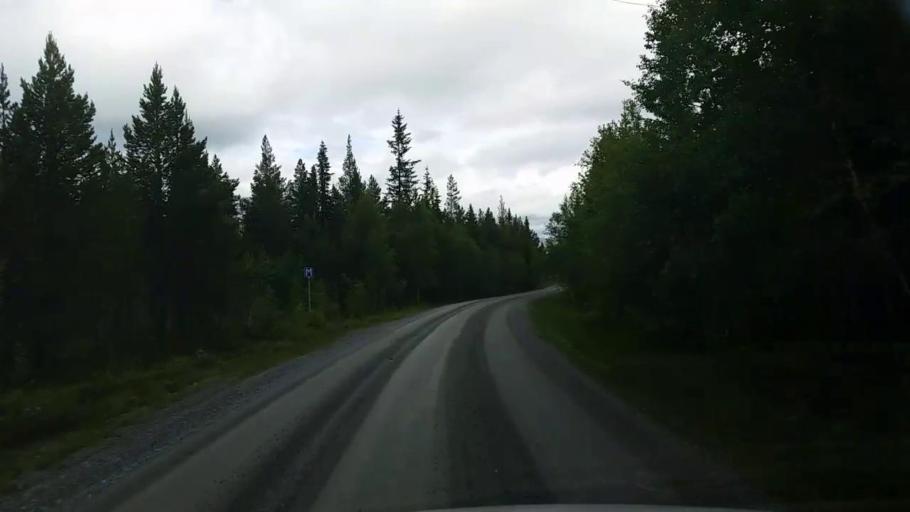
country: NO
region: Hedmark
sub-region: Engerdal
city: Engerdal
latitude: 62.4053
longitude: 12.6647
